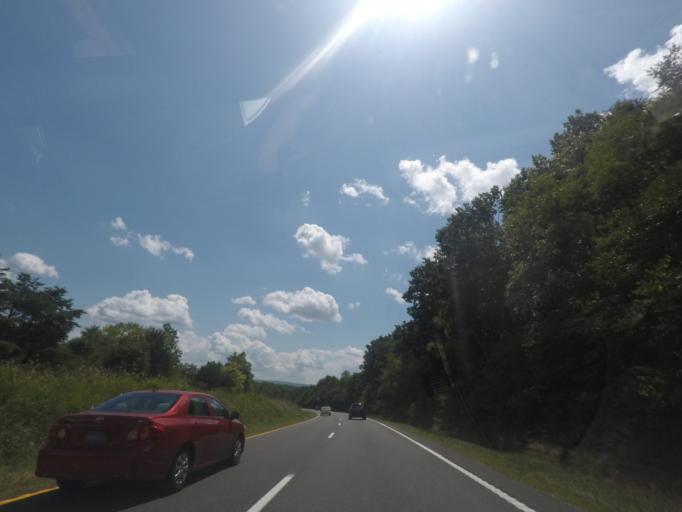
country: US
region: Virginia
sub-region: City of Winchester
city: Winchester
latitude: 39.1003
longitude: -78.1124
